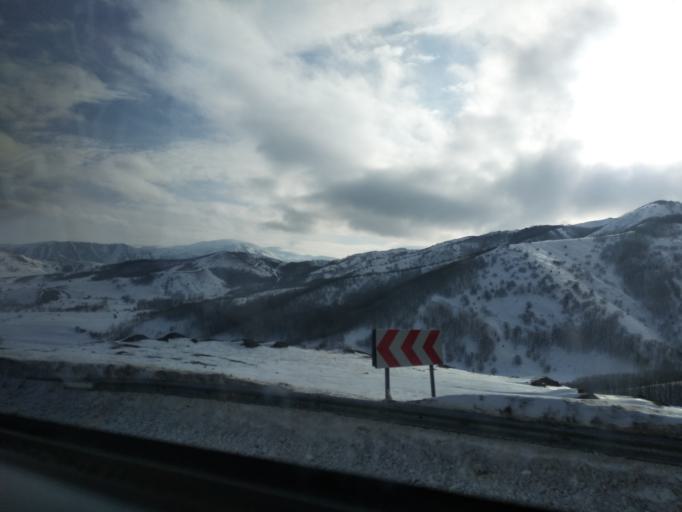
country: TR
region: Erzincan
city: Catalarmut
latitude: 39.8975
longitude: 39.3923
